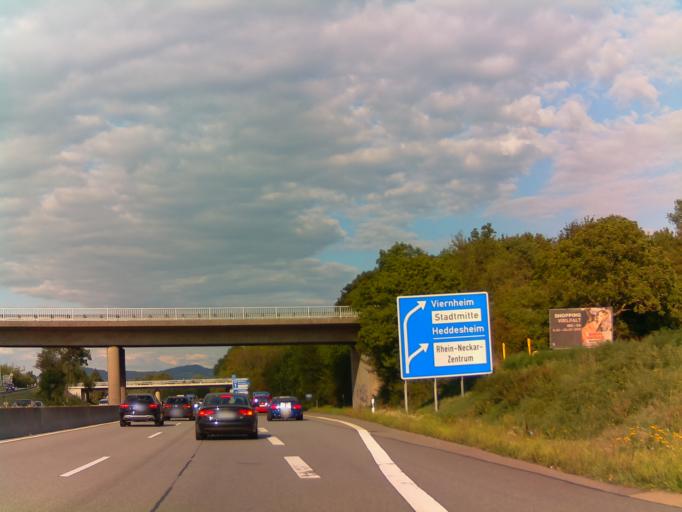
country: DE
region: Hesse
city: Viernheim
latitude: 49.5283
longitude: 8.5770
